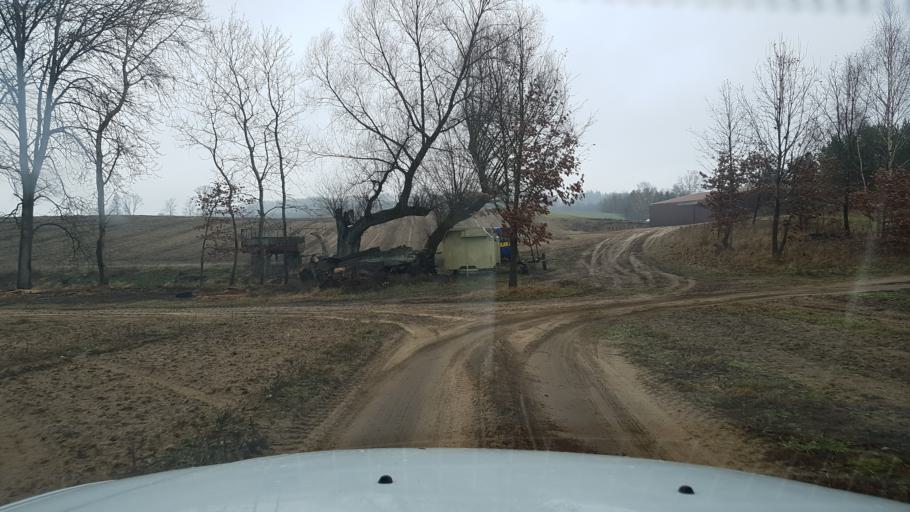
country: PL
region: West Pomeranian Voivodeship
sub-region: Powiat drawski
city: Czaplinek
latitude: 53.5799
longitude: 16.2484
